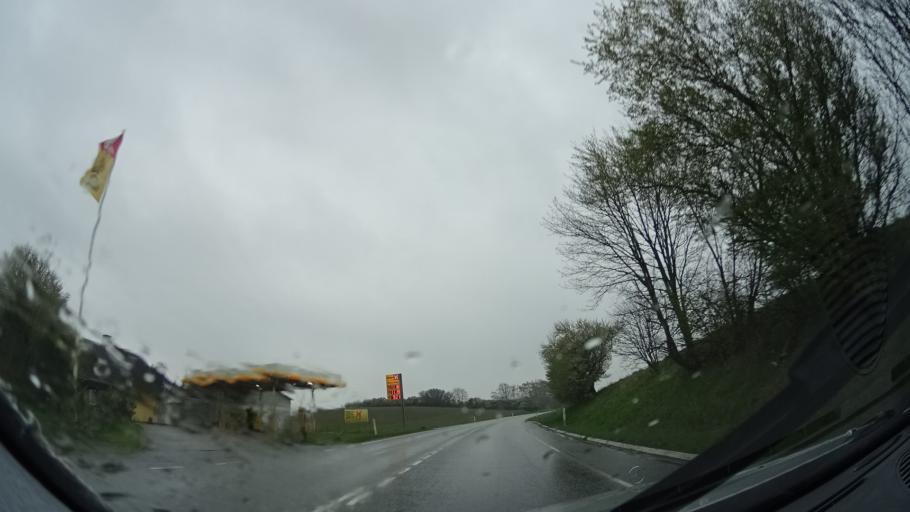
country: DK
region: Zealand
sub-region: Odsherred Kommune
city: Asnaes
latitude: 55.7951
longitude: 11.6020
